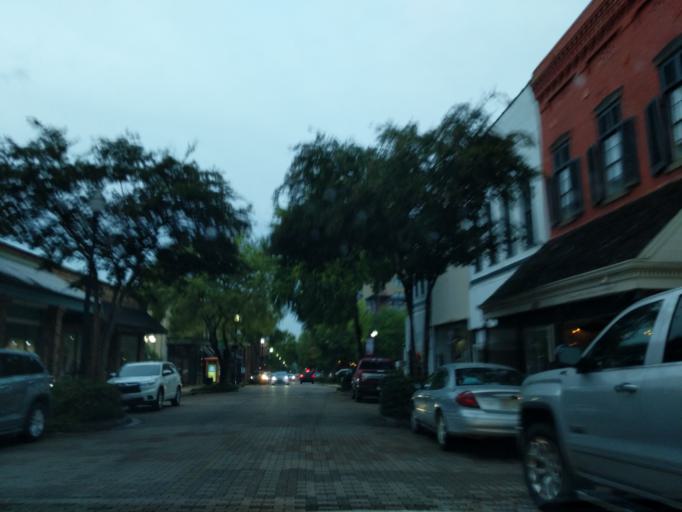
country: US
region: Mississippi
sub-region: Warren County
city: Vicksburg
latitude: 32.3485
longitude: -90.8824
